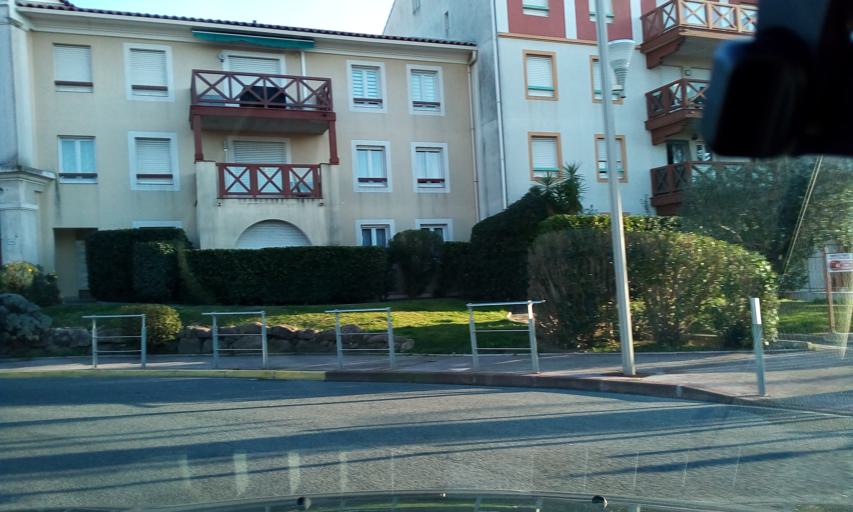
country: FR
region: Provence-Alpes-Cote d'Azur
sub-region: Departement du Var
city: Frejus
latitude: 43.4250
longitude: 6.7461
